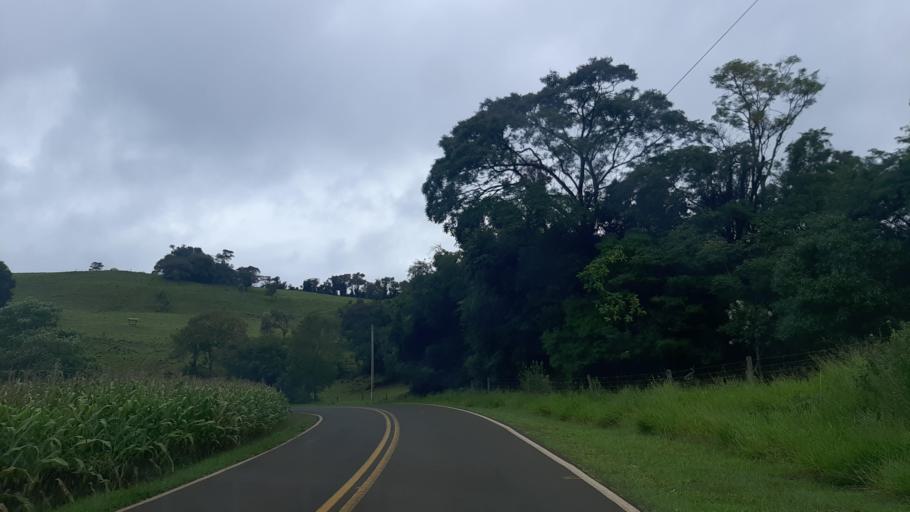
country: BR
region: Parana
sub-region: Ampere
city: Ampere
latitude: -25.9831
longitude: -53.4441
